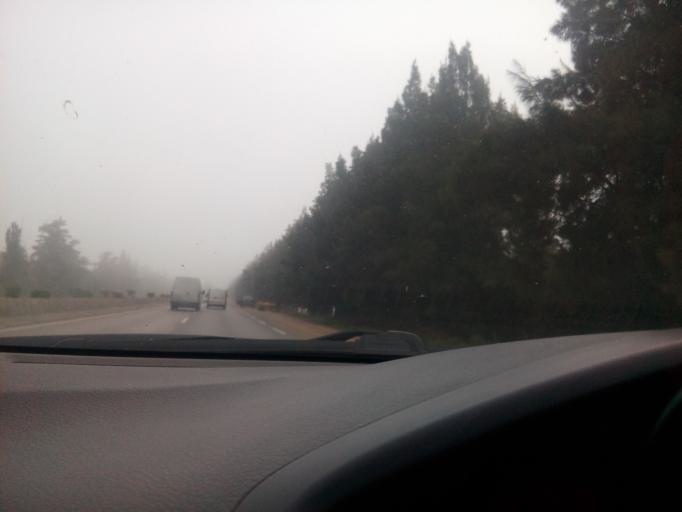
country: DZ
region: Oran
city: Bou Tlelis
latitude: 35.5815
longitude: -0.8292
